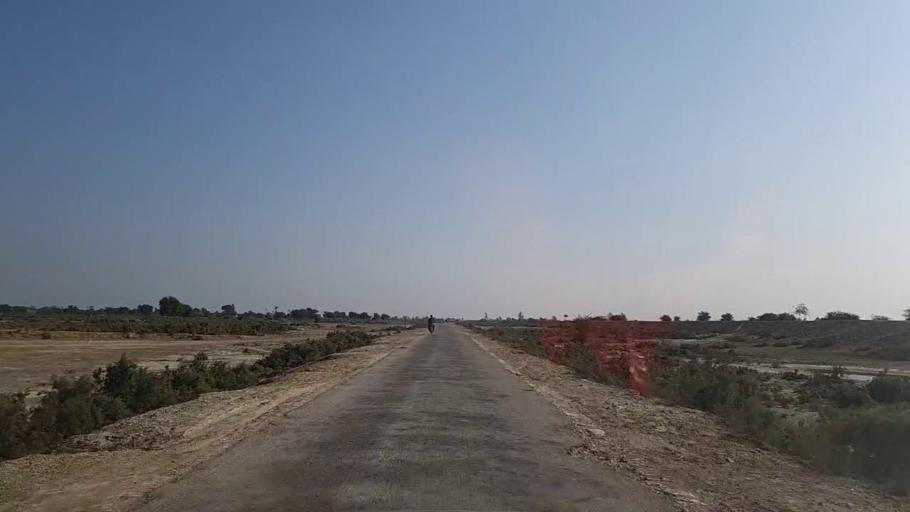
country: PK
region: Sindh
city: Sanghar
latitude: 25.9635
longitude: 69.0371
